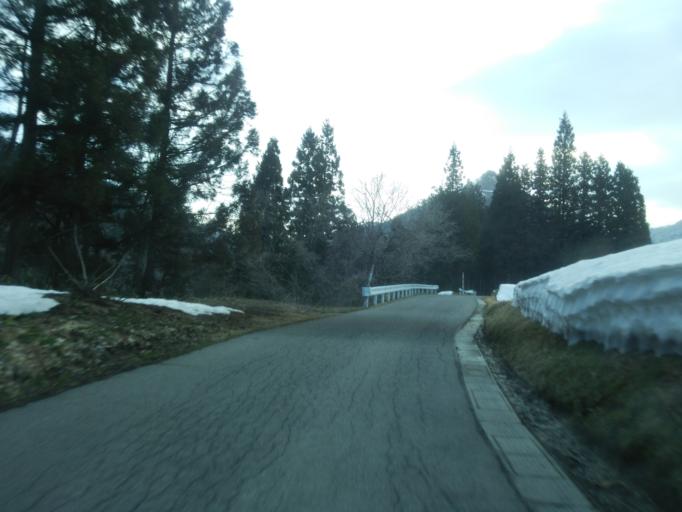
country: JP
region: Fukushima
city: Kitakata
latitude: 37.7308
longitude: 139.9484
